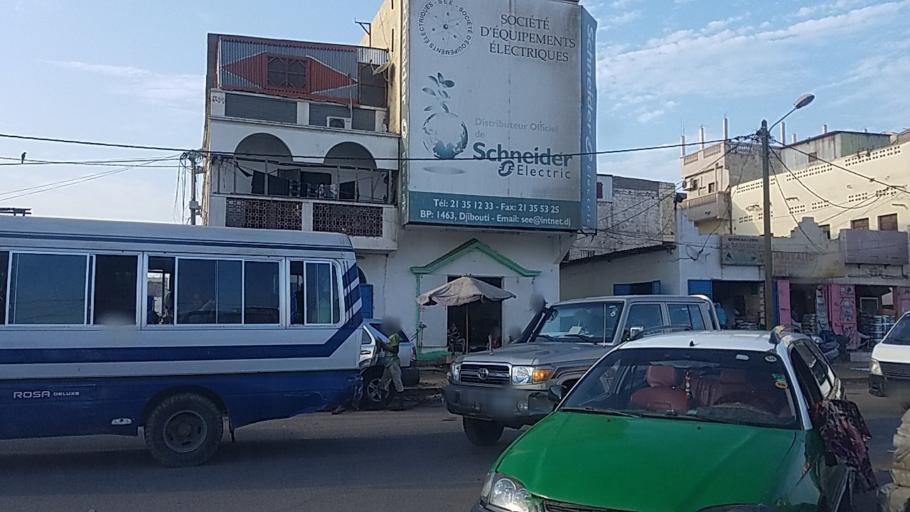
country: DJ
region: Djibouti
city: Djibouti
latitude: 11.5890
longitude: 43.1482
